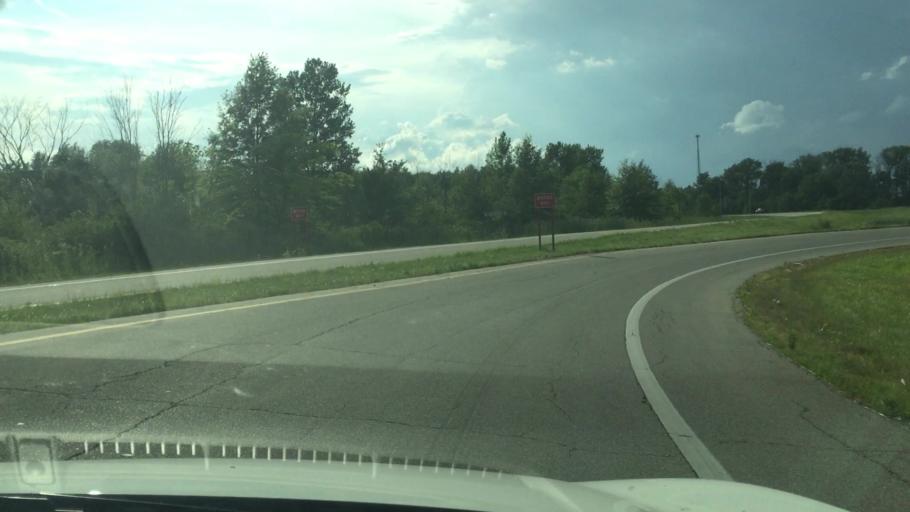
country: US
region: Ohio
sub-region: Champaign County
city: North Lewisburg
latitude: 40.2670
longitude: -83.5008
